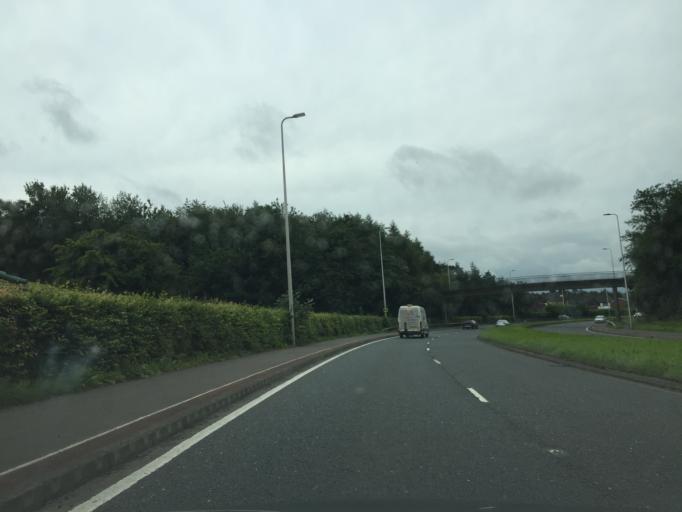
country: GB
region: Northern Ireland
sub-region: Castlereagh District
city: Castlereagh
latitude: 54.6052
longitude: -5.8547
